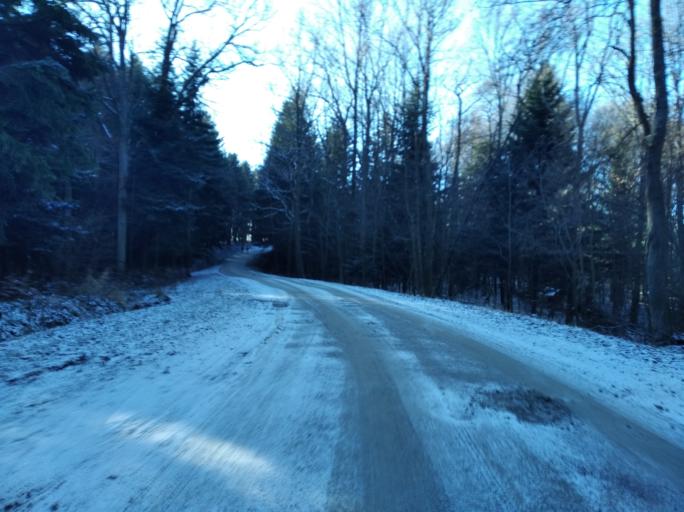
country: PL
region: Subcarpathian Voivodeship
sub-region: Powiat strzyzowski
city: Czudec
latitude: 49.9727
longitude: 21.7916
